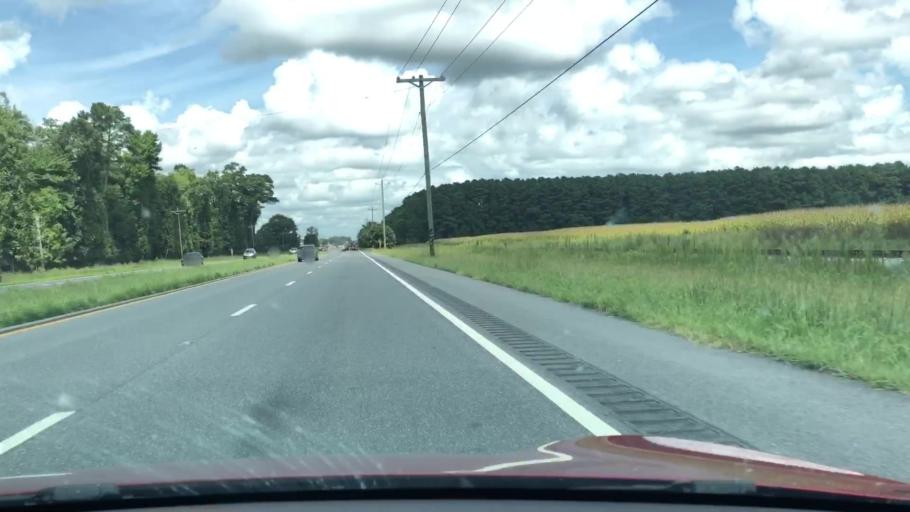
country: US
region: Virginia
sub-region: Northampton County
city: Exmore
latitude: 37.5057
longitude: -75.8381
